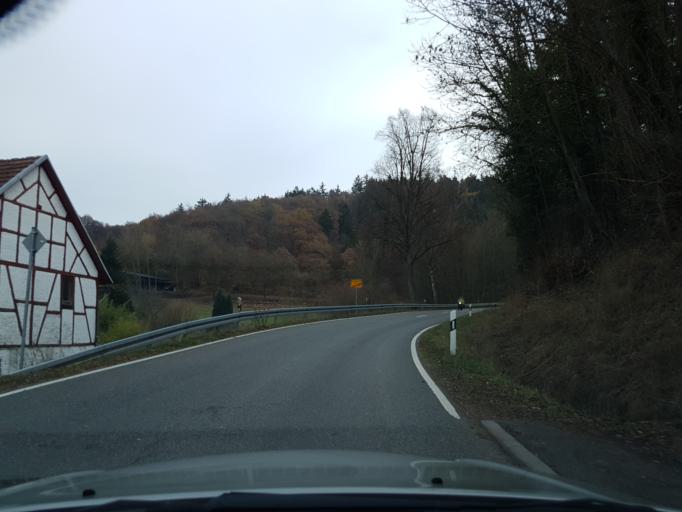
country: DE
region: Hesse
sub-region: Regierungsbezirk Darmstadt
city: Bad Schwalbach
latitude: 50.1336
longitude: 8.0365
